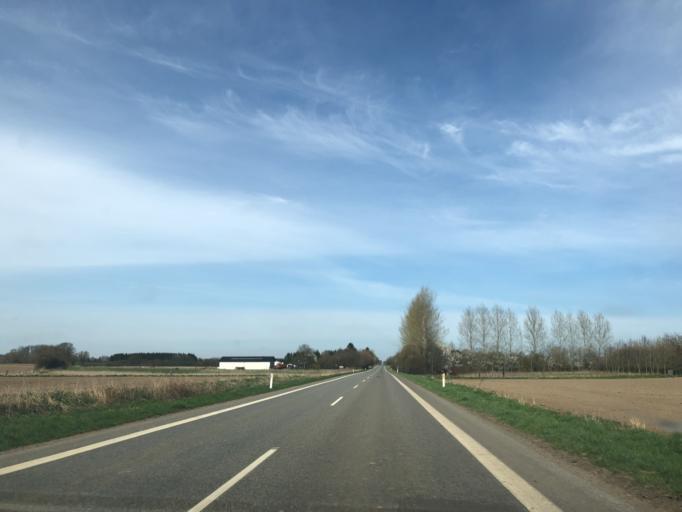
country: DK
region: Zealand
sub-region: Faxe Kommune
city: Ronnede
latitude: 55.2894
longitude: 12.0385
